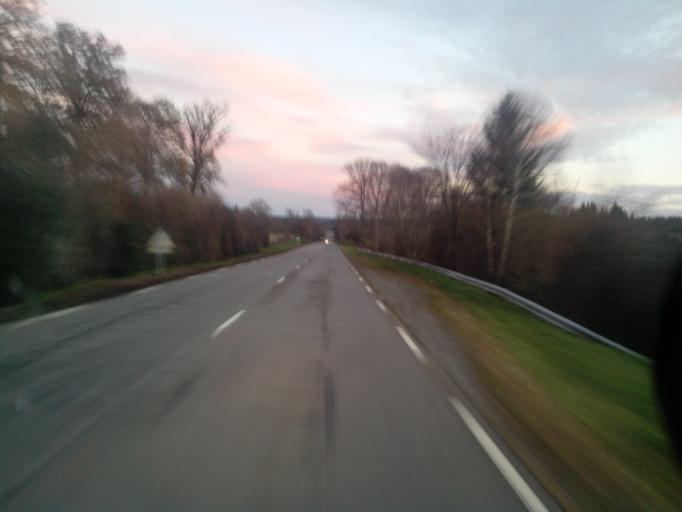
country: FR
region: Limousin
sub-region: Departement de la Correze
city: Meymac
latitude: 45.5111
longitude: 2.1917
